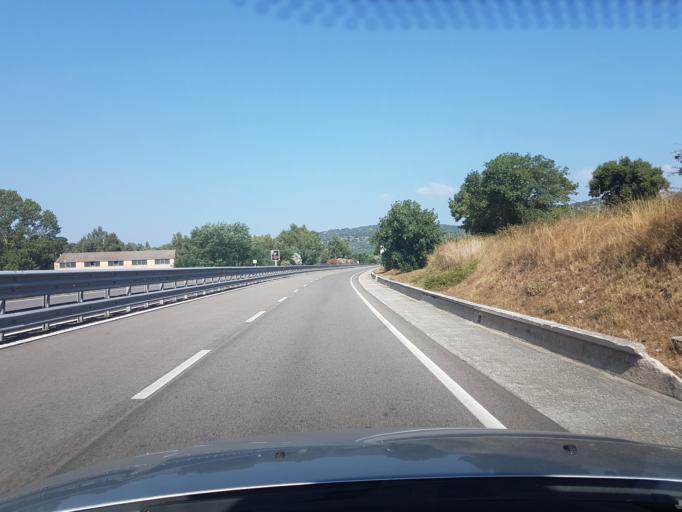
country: IT
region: Sardinia
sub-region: Provincia di Nuoro
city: Oniferi
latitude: 40.3138
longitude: 9.2341
